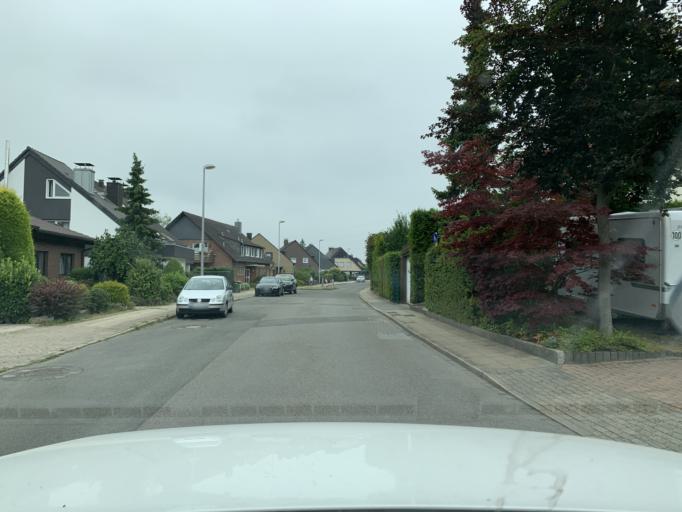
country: DE
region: North Rhine-Westphalia
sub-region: Regierungsbezirk Dusseldorf
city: Muelheim (Ruhr)
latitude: 51.3923
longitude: 6.8680
